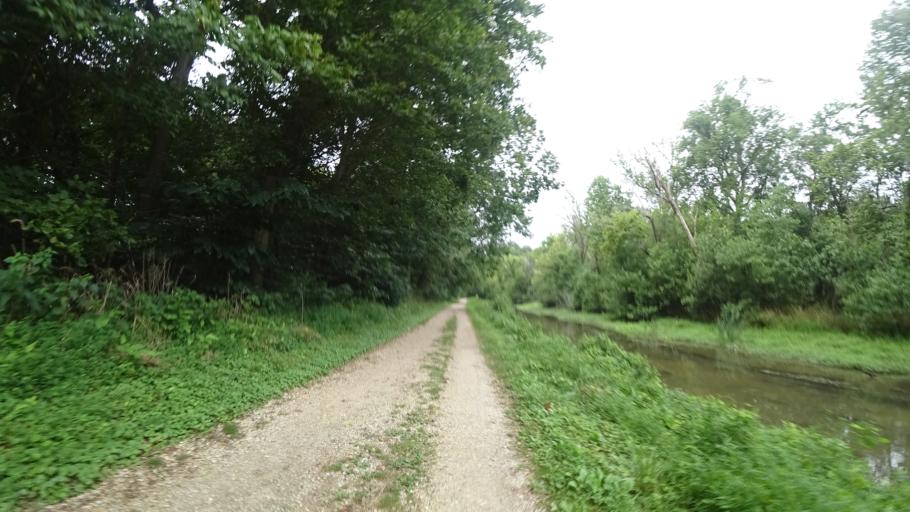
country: US
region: Maryland
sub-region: Montgomery County
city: Travilah
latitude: 39.0394
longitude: -77.2587
